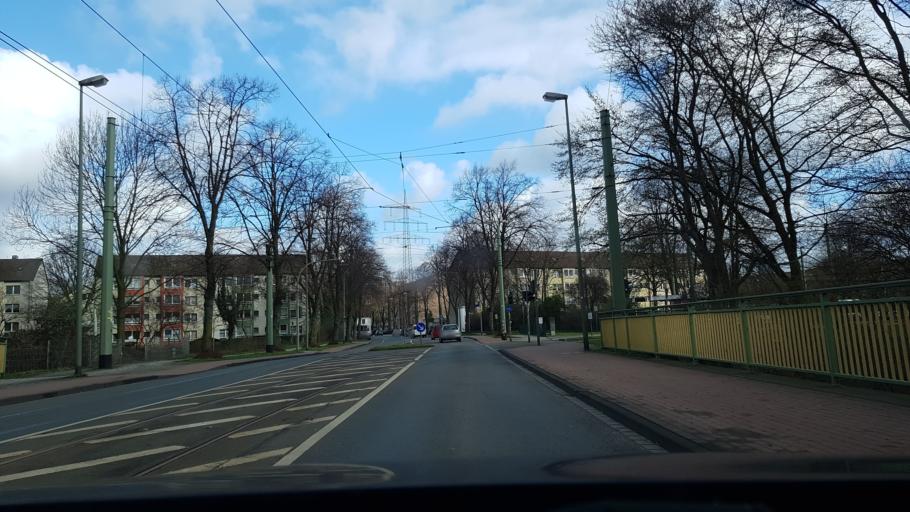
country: DE
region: North Rhine-Westphalia
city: Meiderich
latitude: 51.5062
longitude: 6.7856
